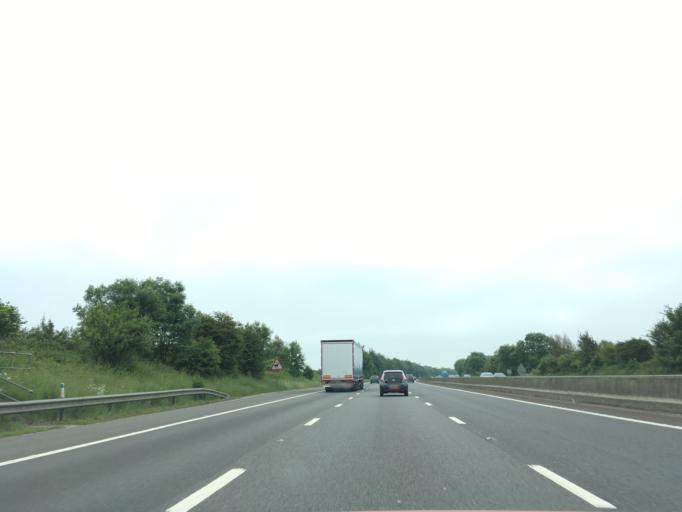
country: GB
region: England
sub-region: West Berkshire
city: Lambourn
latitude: 51.4710
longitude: -1.5257
